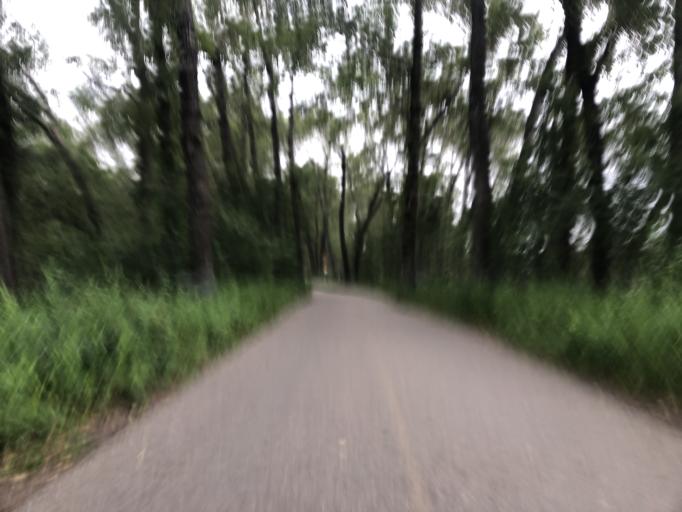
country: CA
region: Alberta
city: Calgary
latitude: 51.0433
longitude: -114.0162
